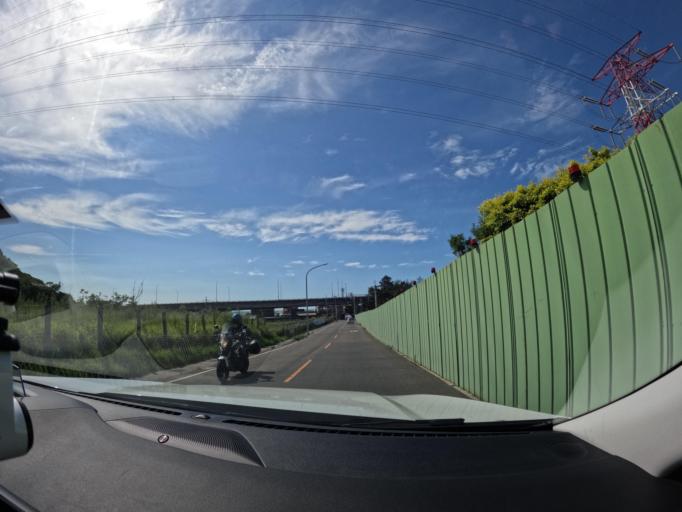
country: TW
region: Taiwan
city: Taoyuan City
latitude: 25.1193
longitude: 121.2969
